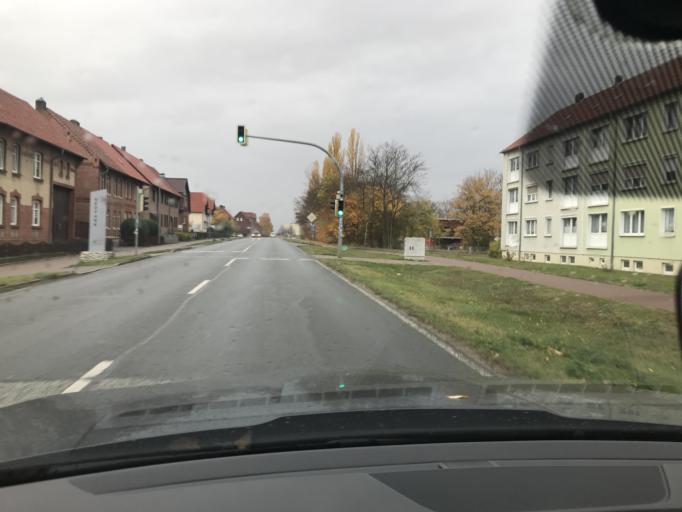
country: DE
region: Saxony-Anhalt
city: Harsleben
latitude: 51.8715
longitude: 11.0948
